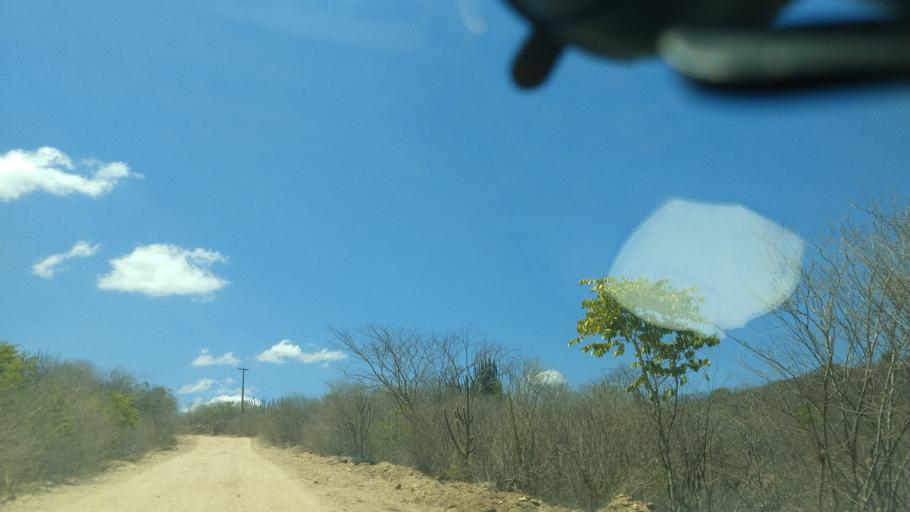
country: BR
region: Rio Grande do Norte
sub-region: Cerro Cora
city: Cerro Cora
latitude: -6.0119
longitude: -36.3247
